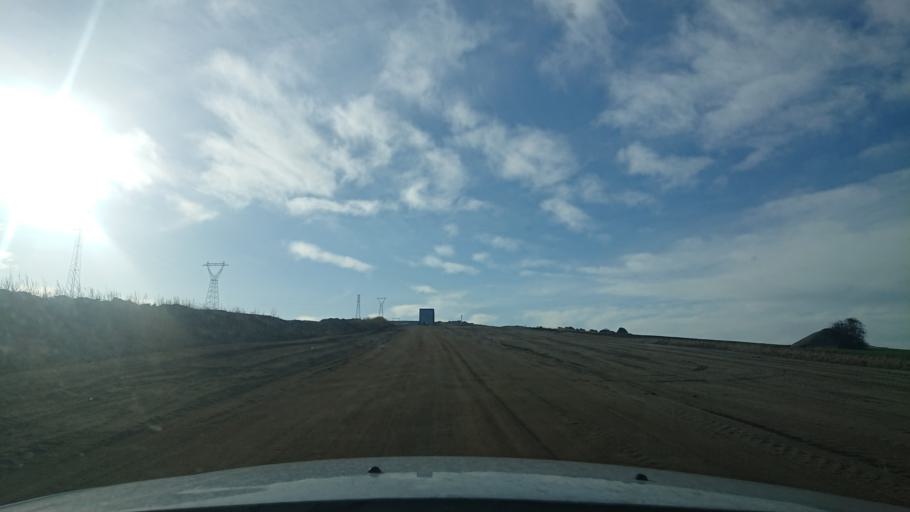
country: TR
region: Aksaray
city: Agacoren
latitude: 38.8503
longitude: 33.9428
